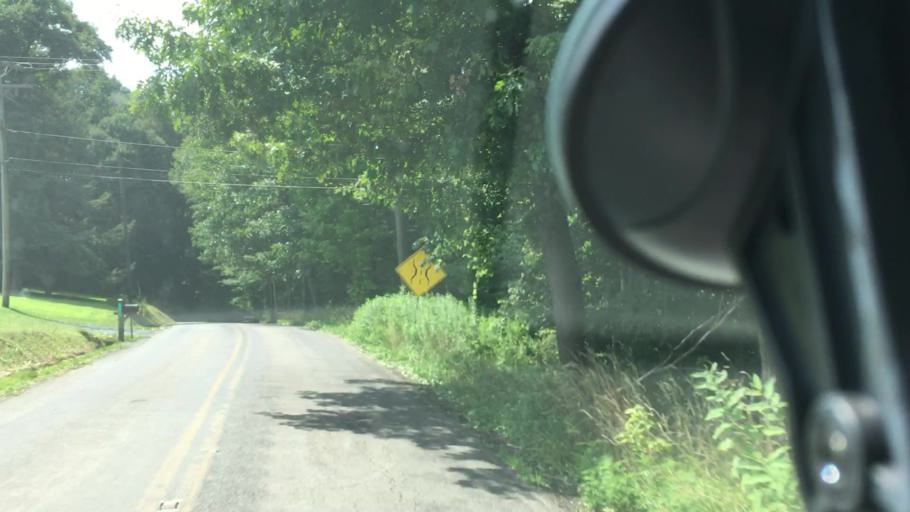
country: US
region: Pennsylvania
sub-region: Mercer County
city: Reynolds Heights
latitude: 41.3075
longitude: -80.3812
